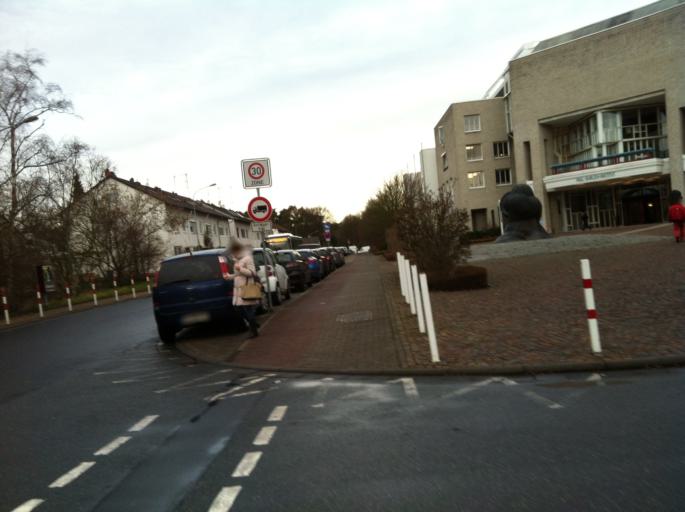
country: DE
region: Hesse
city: Langen
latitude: 50.0049
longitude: 8.6504
